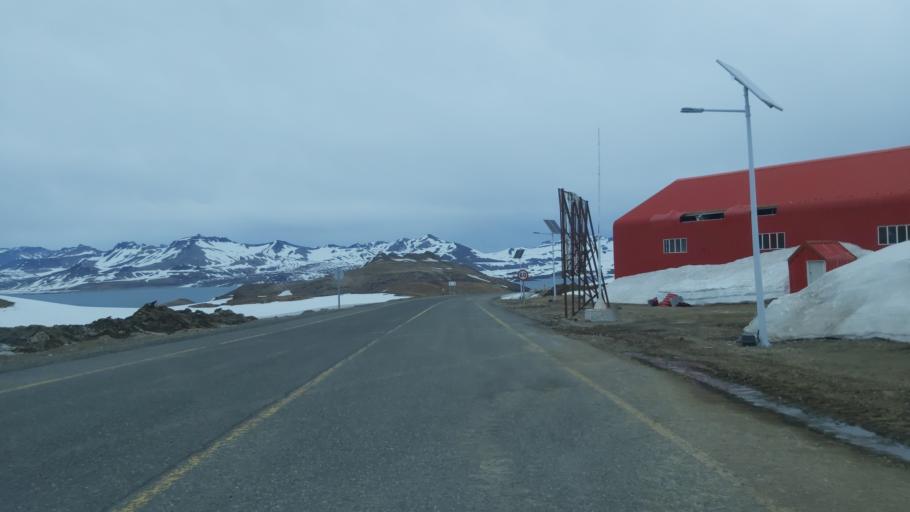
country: CL
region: Maule
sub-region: Provincia de Linares
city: Colbun
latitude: -36.0104
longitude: -70.4827
